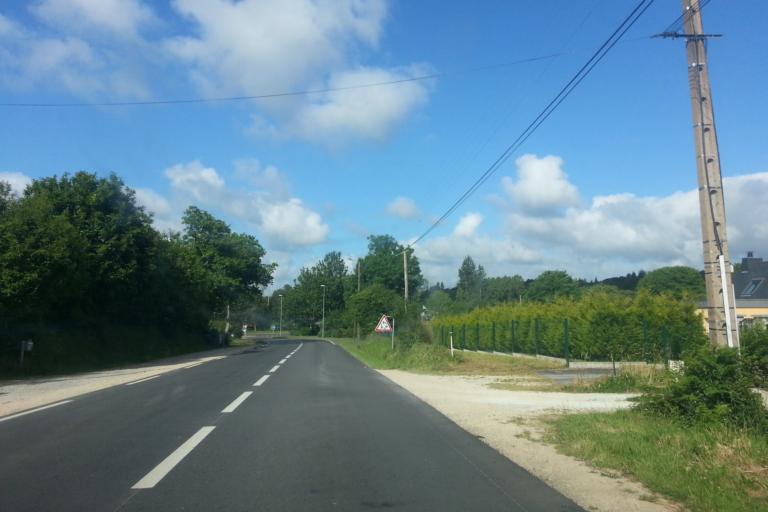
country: FR
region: Brittany
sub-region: Departement du Finistere
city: Scaer
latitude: 48.0243
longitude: -3.6835
